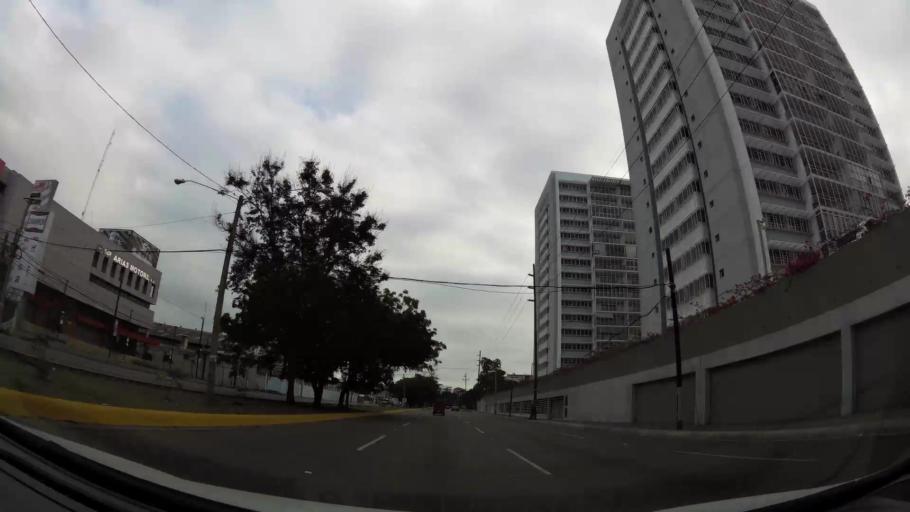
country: DO
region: Nacional
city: Bella Vista
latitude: 18.4384
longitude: -69.9806
